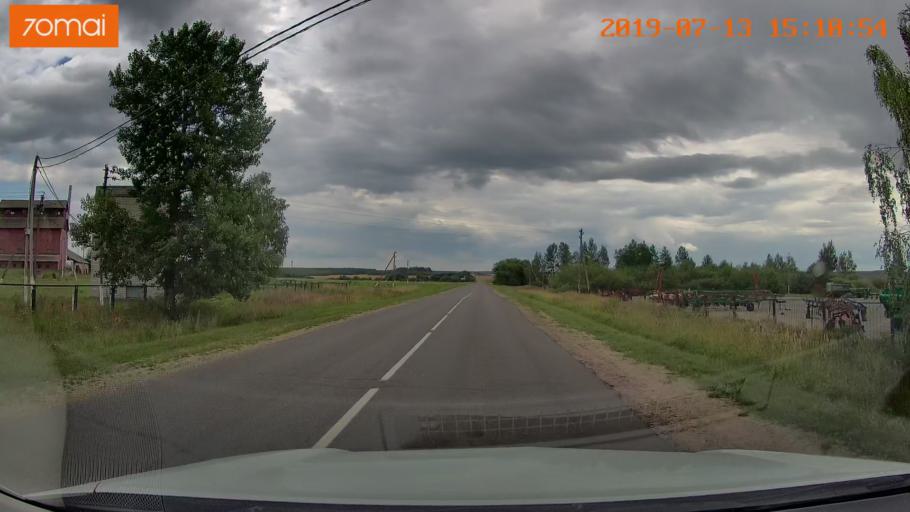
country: BY
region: Mogilev
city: Hlusha
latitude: 53.1676
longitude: 28.7801
